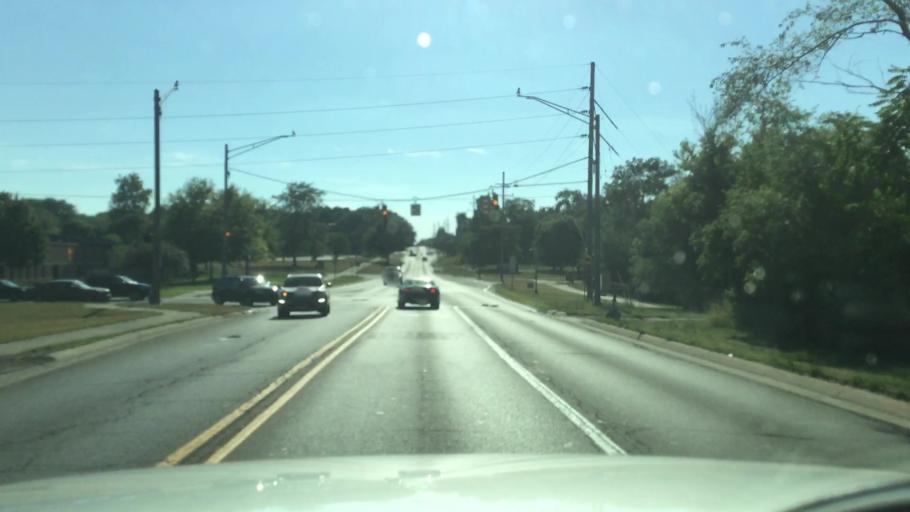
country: US
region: Michigan
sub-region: Oakland County
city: Waterford
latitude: 42.6750
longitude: -83.3862
